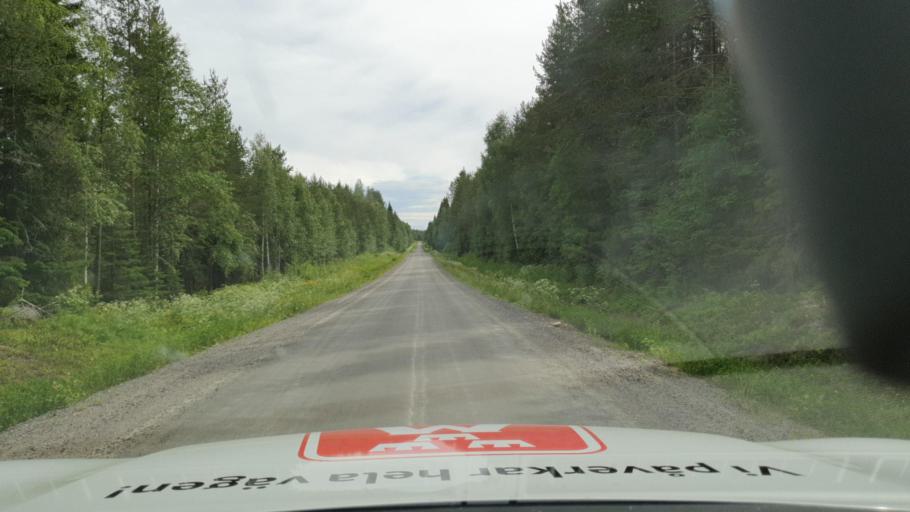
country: SE
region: Vaesterbotten
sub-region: Skelleftea Kommun
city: Burea
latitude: 64.4364
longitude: 21.0161
